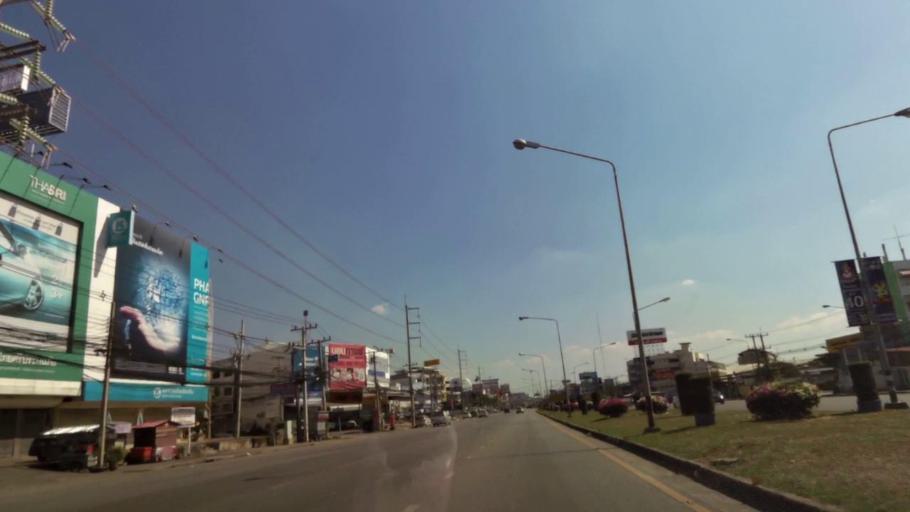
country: TH
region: Nakhon Sawan
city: Nakhon Sawan
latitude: 15.7040
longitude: 100.1145
